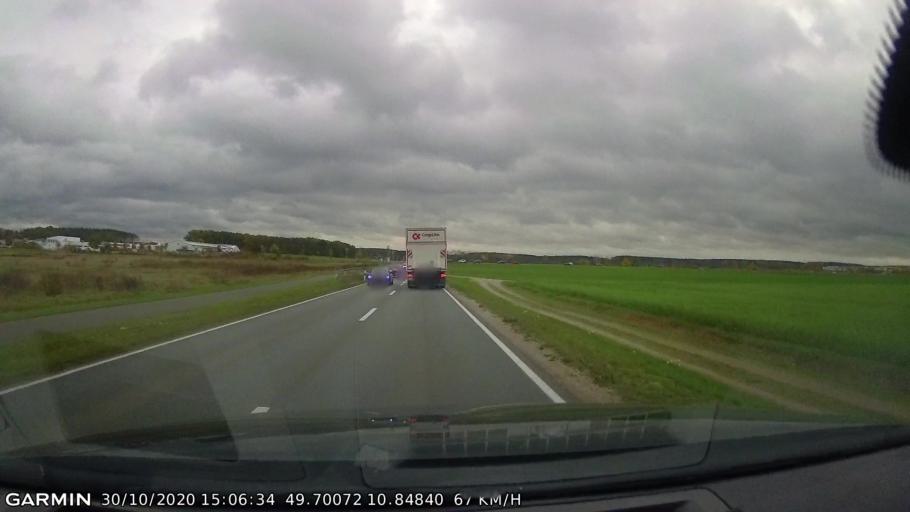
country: DE
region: Bavaria
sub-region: Regierungsbezirk Mittelfranken
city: Gremsdorf
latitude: 49.7006
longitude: 10.8484
